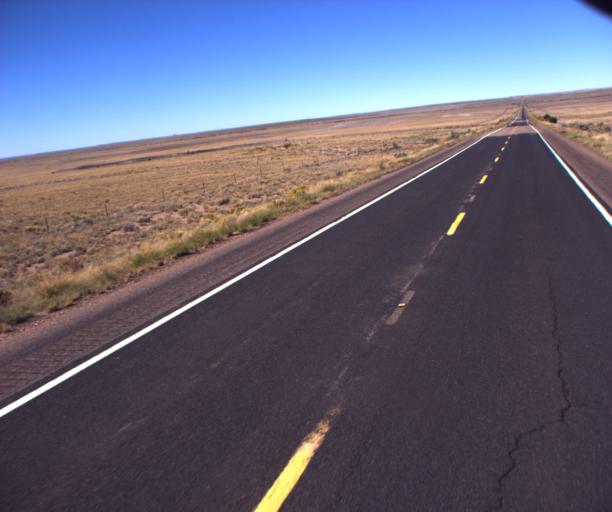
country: US
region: Arizona
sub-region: Navajo County
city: Snowflake
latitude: 34.7193
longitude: -109.7713
